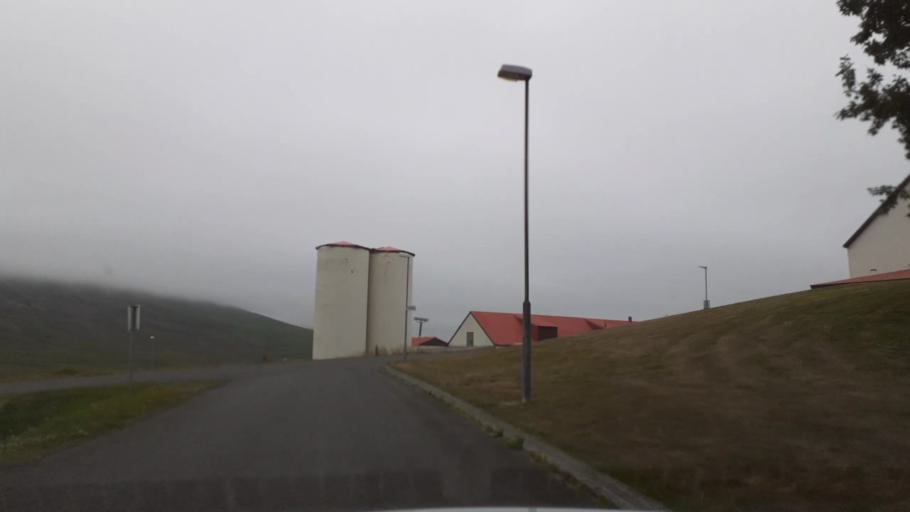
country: IS
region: Northeast
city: Siglufjoerdur
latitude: 65.7324
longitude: -19.1113
